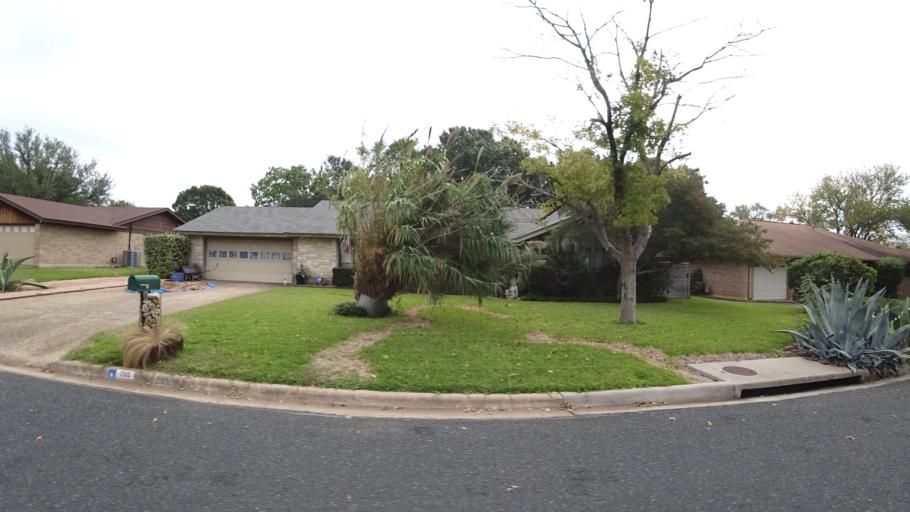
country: US
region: Texas
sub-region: Travis County
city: Shady Hollow
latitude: 30.2140
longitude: -97.8368
